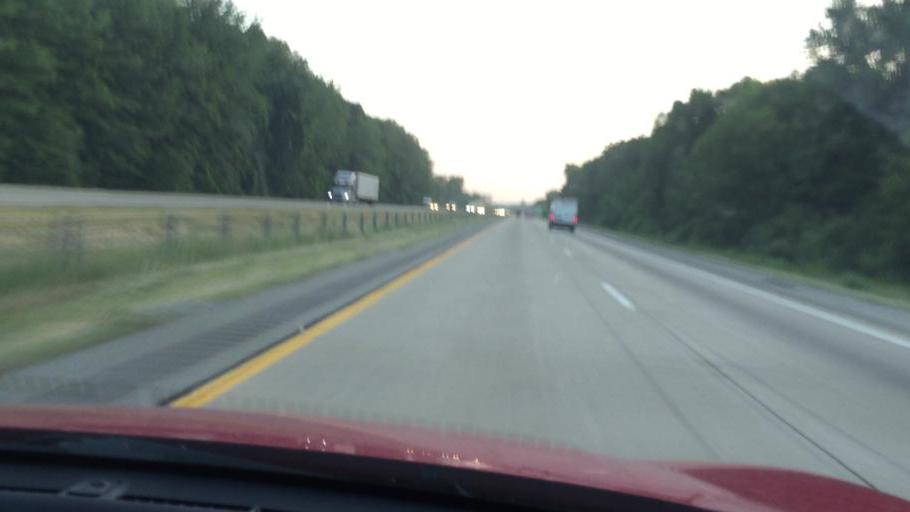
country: US
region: Michigan
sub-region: Monroe County
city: Dundee
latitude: 41.9246
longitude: -83.6622
